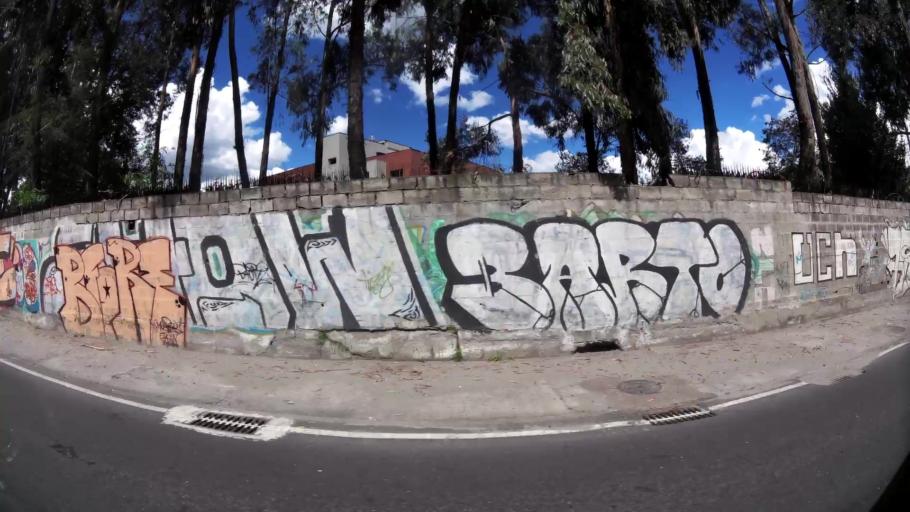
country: EC
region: Pichincha
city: Quito
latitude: -0.1680
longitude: -78.4985
